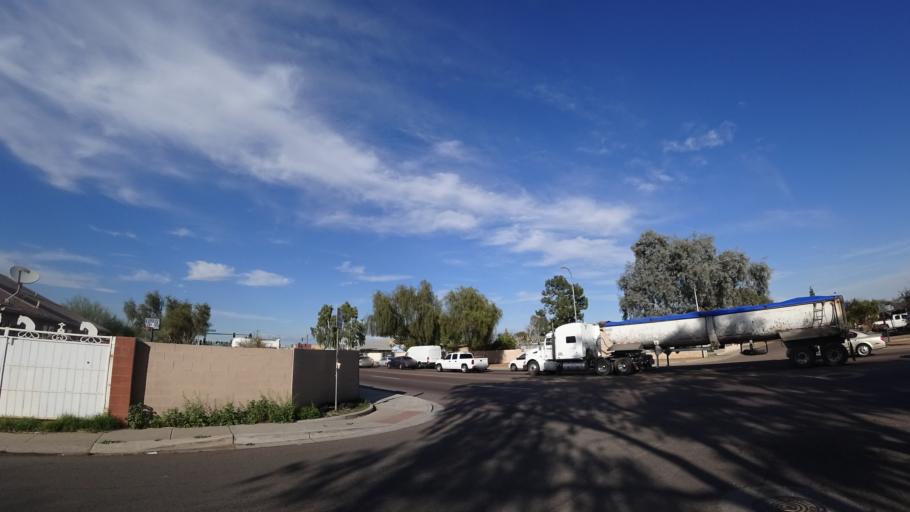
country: US
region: Arizona
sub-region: Maricopa County
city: Tolleson
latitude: 33.4575
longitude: -112.2037
